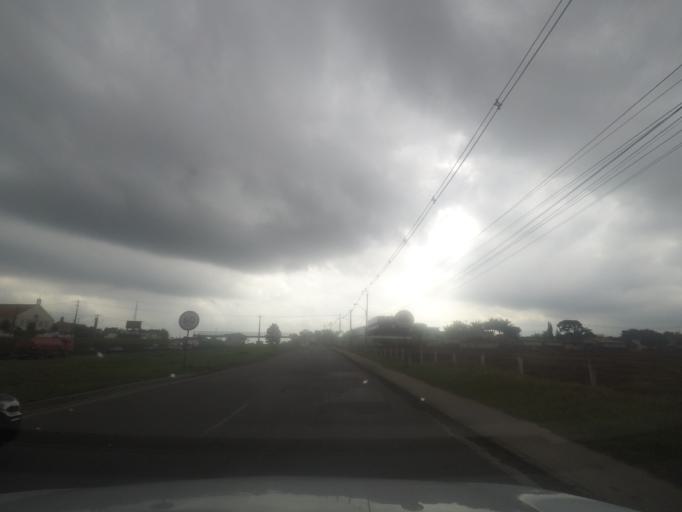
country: BR
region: Parana
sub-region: Sao Jose Dos Pinhais
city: Sao Jose dos Pinhais
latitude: -25.5481
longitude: -49.2860
